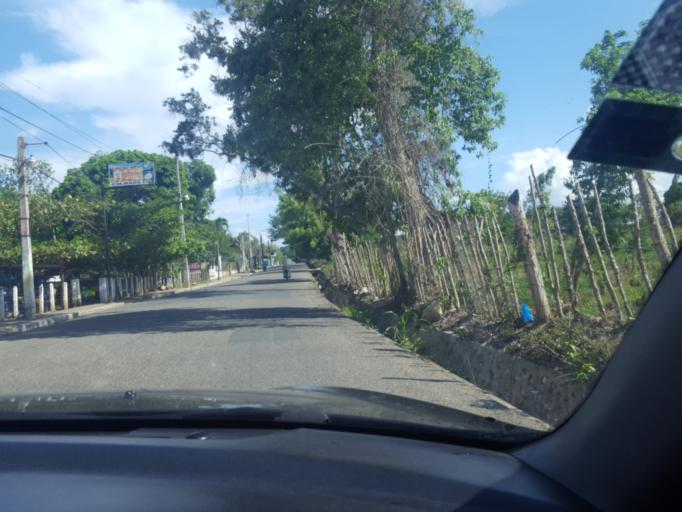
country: DO
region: La Vega
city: Rio Verde Arriba
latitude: 19.3666
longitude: -70.6052
